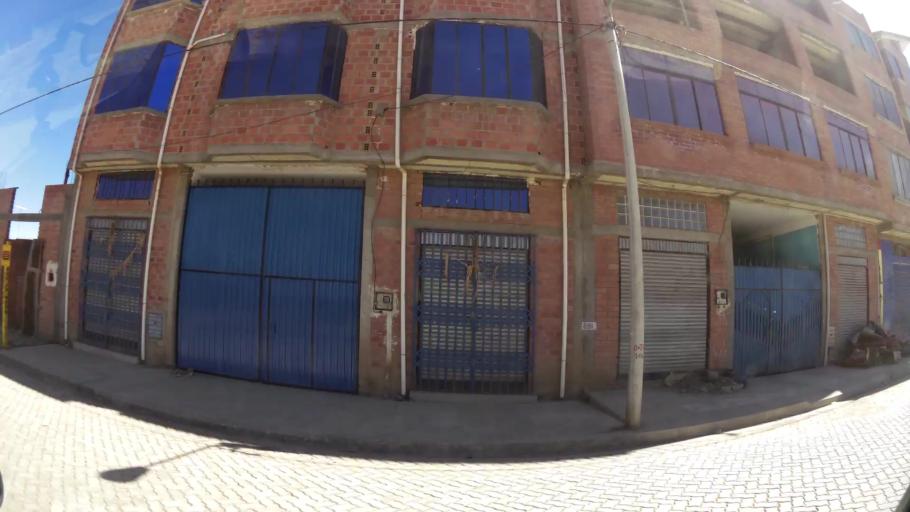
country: BO
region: La Paz
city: La Paz
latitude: -16.5396
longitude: -68.1966
